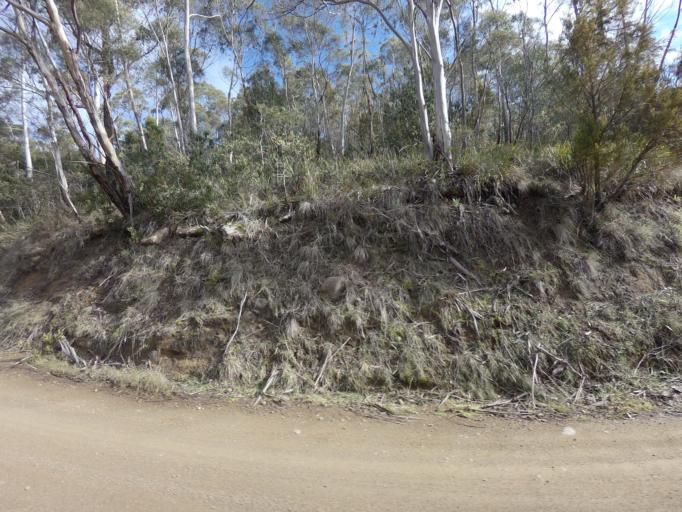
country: AU
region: Tasmania
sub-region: Derwent Valley
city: New Norfolk
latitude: -42.7901
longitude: 146.9392
